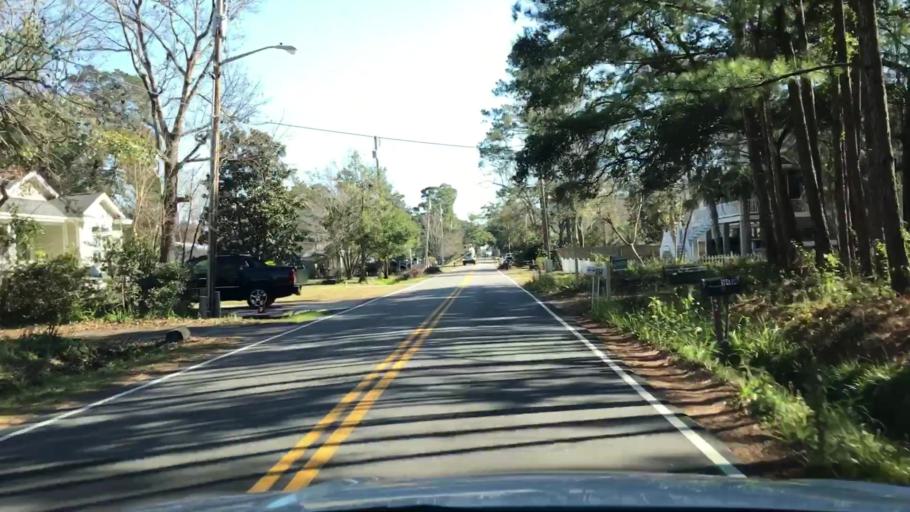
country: US
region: South Carolina
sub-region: Horry County
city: Garden City
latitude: 33.5925
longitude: -78.9993
